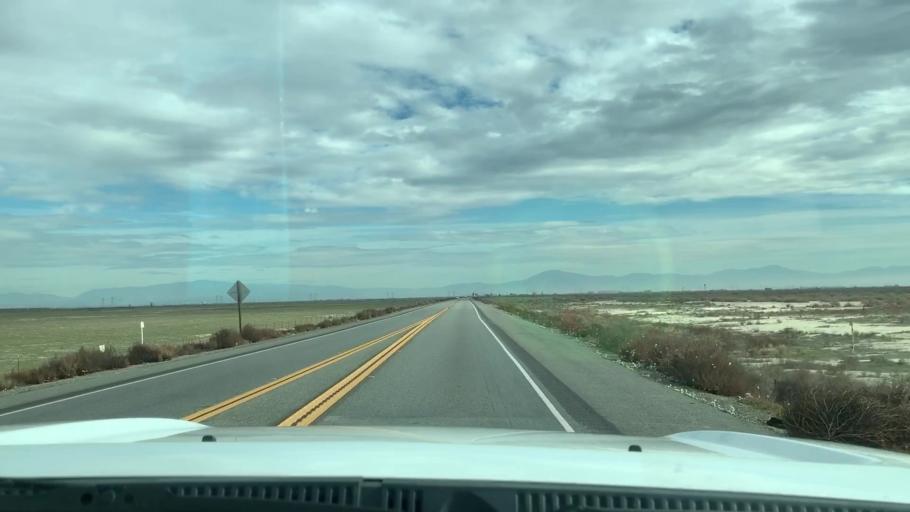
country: US
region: California
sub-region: Kern County
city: Rosedale
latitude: 35.2675
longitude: -119.2863
